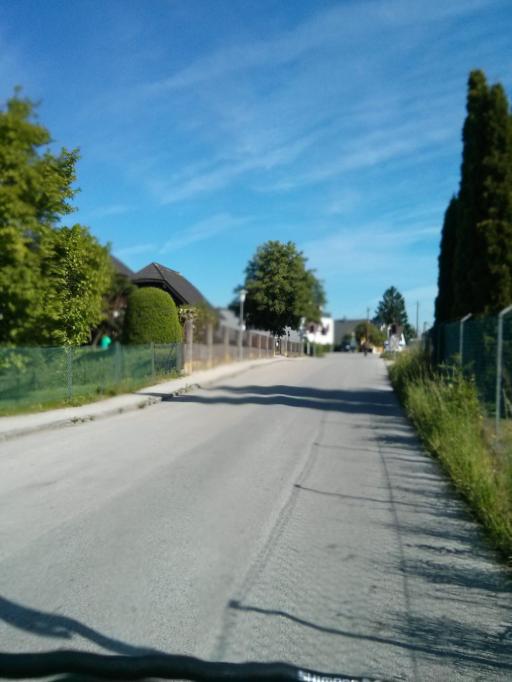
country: AT
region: Salzburg
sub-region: Politischer Bezirk Salzburg-Umgebung
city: Bergheim
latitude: 47.8096
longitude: 13.0165
